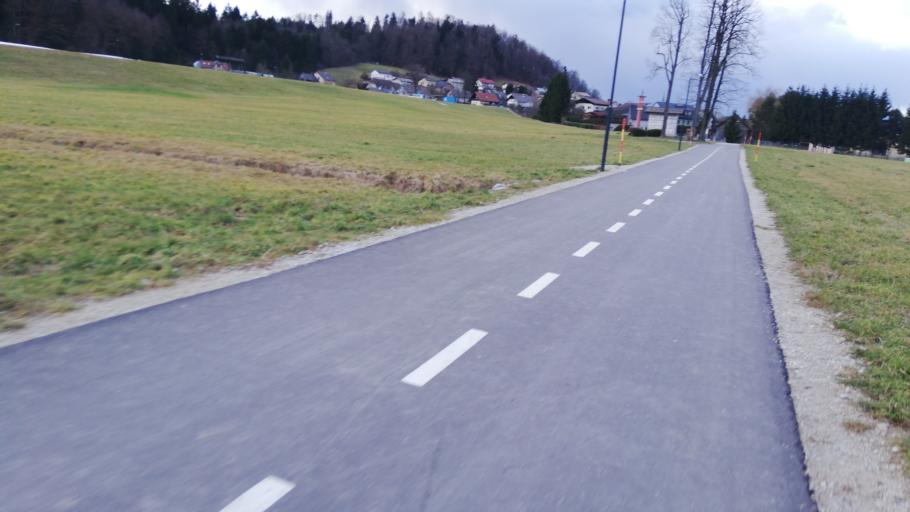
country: SI
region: Medvode
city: Medvode
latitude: 46.1279
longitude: 14.4159
